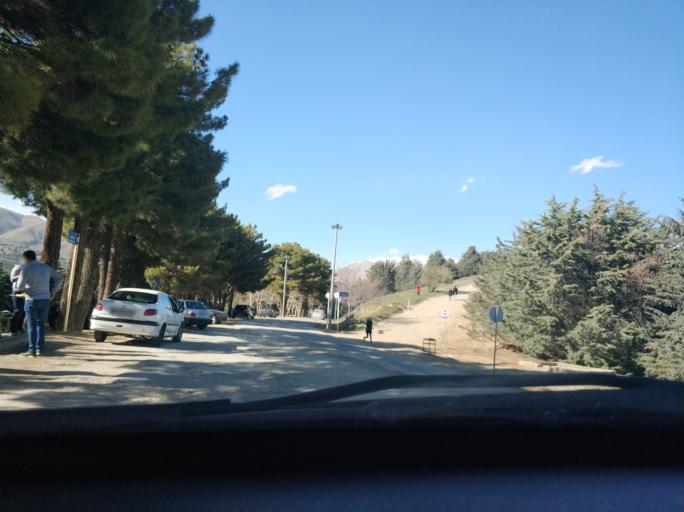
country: IR
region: Tehran
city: Tajrish
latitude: 35.8006
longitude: 51.5675
